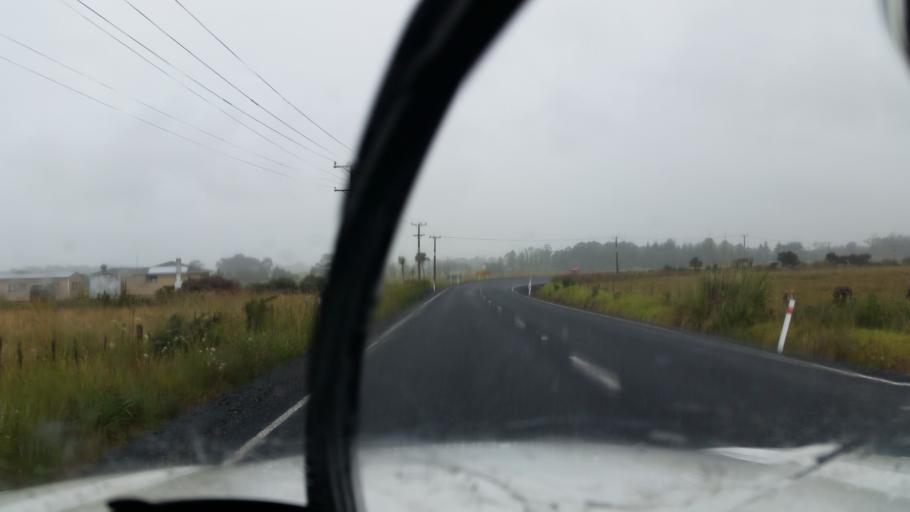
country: NZ
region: Northland
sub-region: Far North District
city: Ahipara
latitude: -35.1802
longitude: 173.1684
